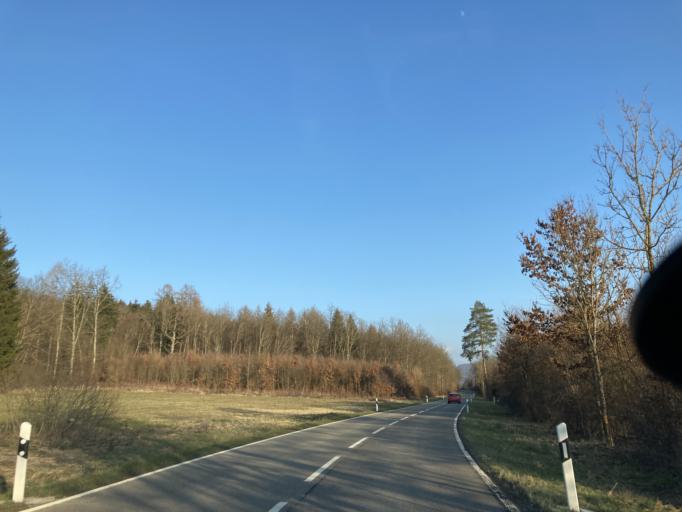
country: DE
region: Baden-Wuerttemberg
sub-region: Tuebingen Region
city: Ofterdingen
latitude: 48.4213
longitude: 8.9983
